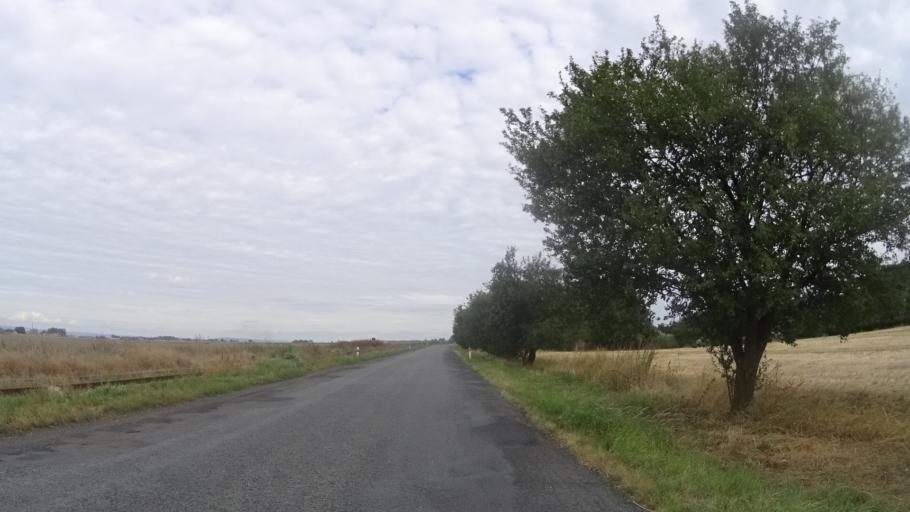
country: CZ
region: Olomoucky
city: Tovacov
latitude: 49.4070
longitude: 17.2845
